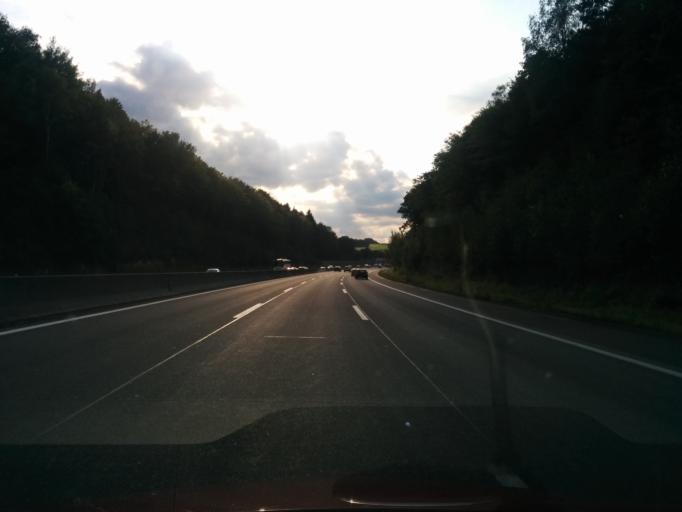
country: AT
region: Lower Austria
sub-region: Politischer Bezirk Amstetten
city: Sankt Georgen am Ybbsfelde
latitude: 48.1385
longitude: 14.9336
